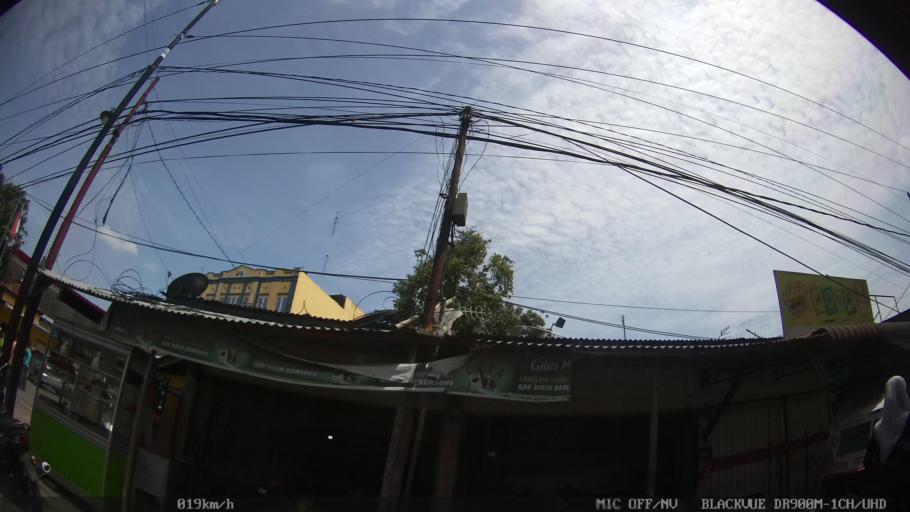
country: ID
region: North Sumatra
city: Sunggal
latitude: 3.5784
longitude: 98.6275
